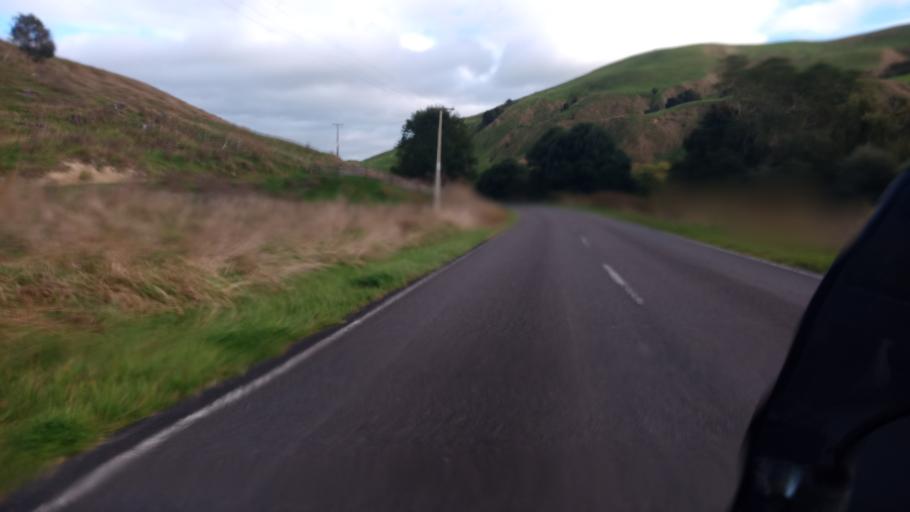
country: NZ
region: Gisborne
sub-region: Gisborne District
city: Gisborne
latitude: -38.5721
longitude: 177.7354
